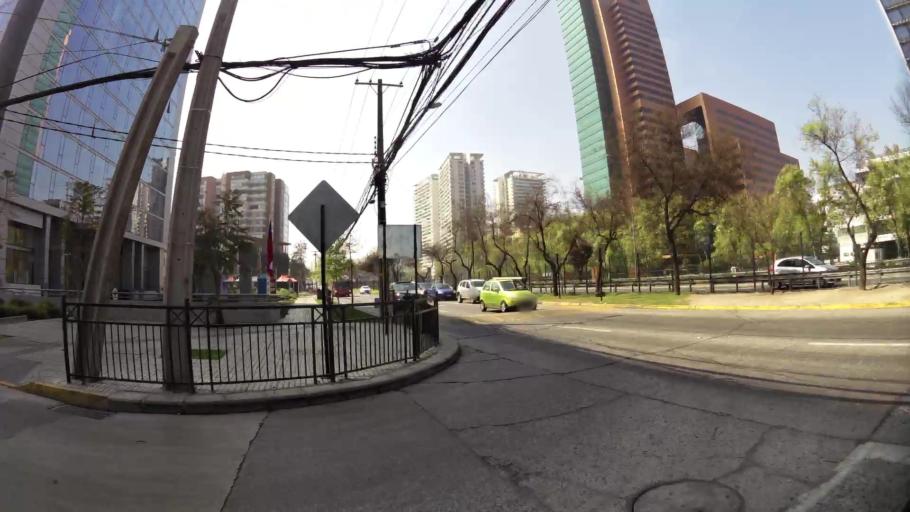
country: CL
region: Santiago Metropolitan
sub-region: Provincia de Santiago
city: Villa Presidente Frei, Nunoa, Santiago, Chile
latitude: -33.3995
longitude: -70.5758
